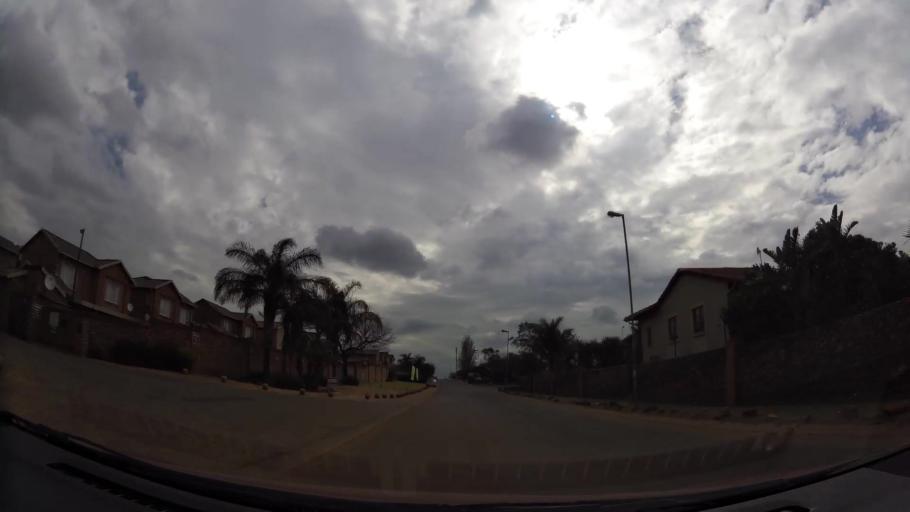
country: ZA
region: Gauteng
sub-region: City of Johannesburg Metropolitan Municipality
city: Roodepoort
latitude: -26.0972
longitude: 27.8792
